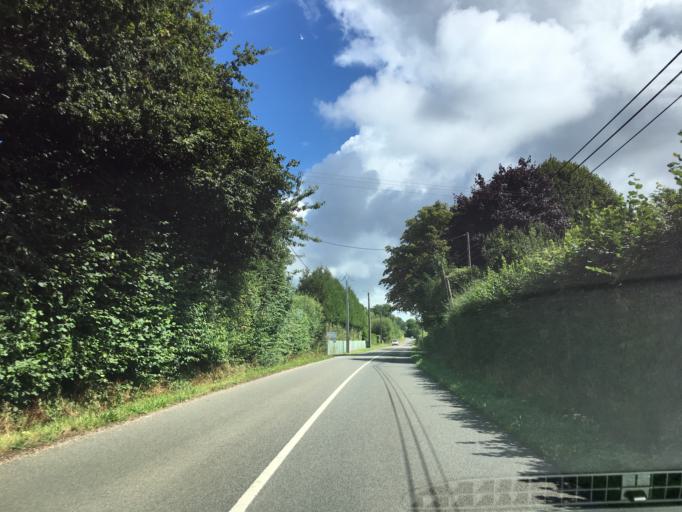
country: FR
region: Lower Normandy
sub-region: Departement du Calvados
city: Houlgate
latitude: 49.2761
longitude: -0.0621
